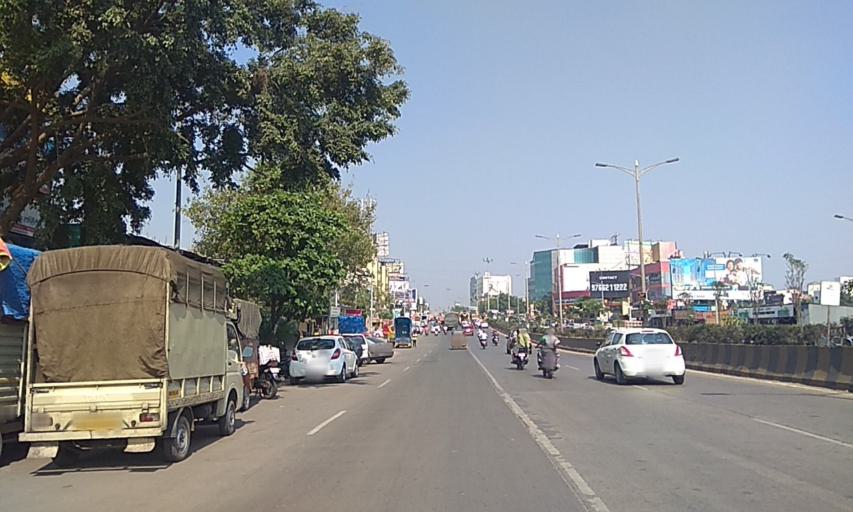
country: IN
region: Maharashtra
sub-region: Pune Division
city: Lohogaon
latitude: 18.5490
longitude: 73.9366
